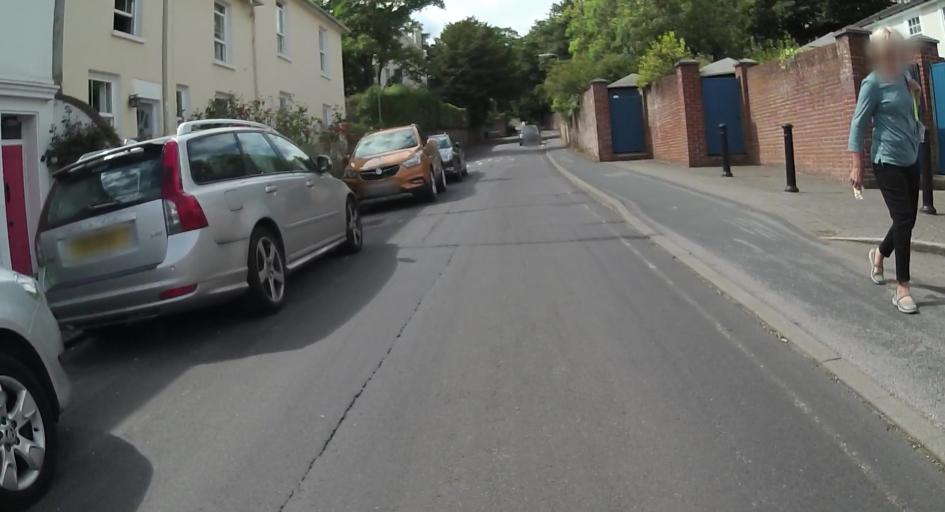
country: GB
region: England
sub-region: Hampshire
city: Winchester
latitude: 51.0603
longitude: -1.3202
